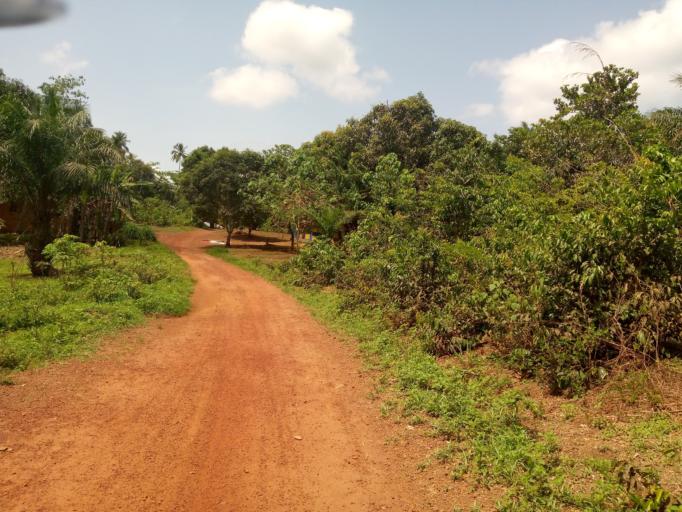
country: SL
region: Western Area
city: Waterloo
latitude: 8.3574
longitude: -12.9253
